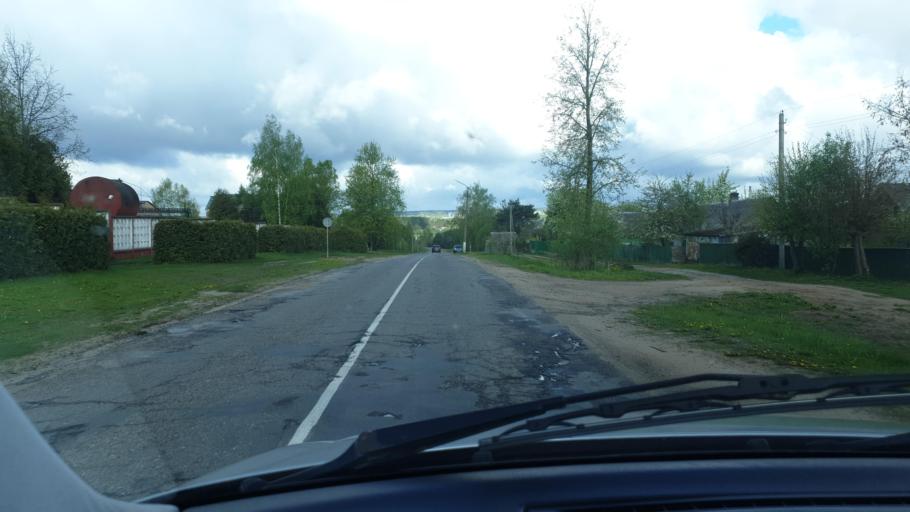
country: BY
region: Vitebsk
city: Lyepyel'
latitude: 54.8754
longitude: 28.6775
